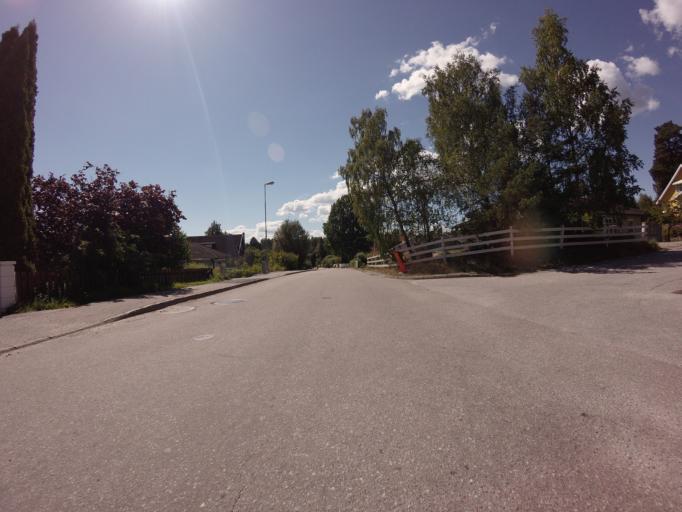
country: SE
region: Stockholm
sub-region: Sollentuna Kommun
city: Sollentuna
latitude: 59.4522
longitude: 17.8953
